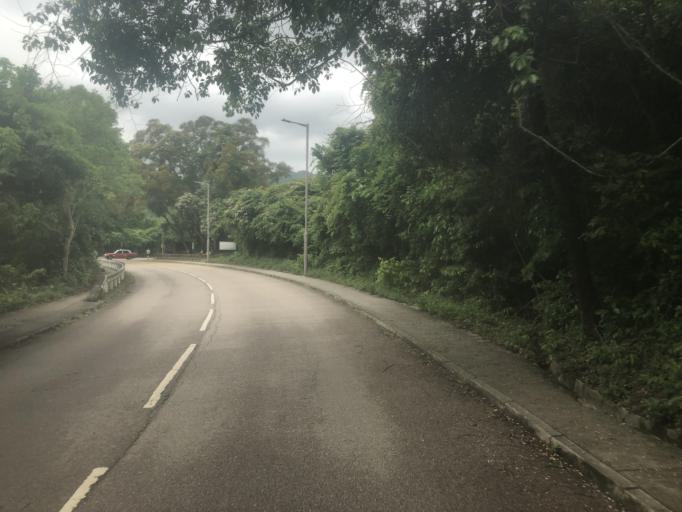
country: HK
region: Sai Kung
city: Sai Kung
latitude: 22.3999
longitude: 114.3246
